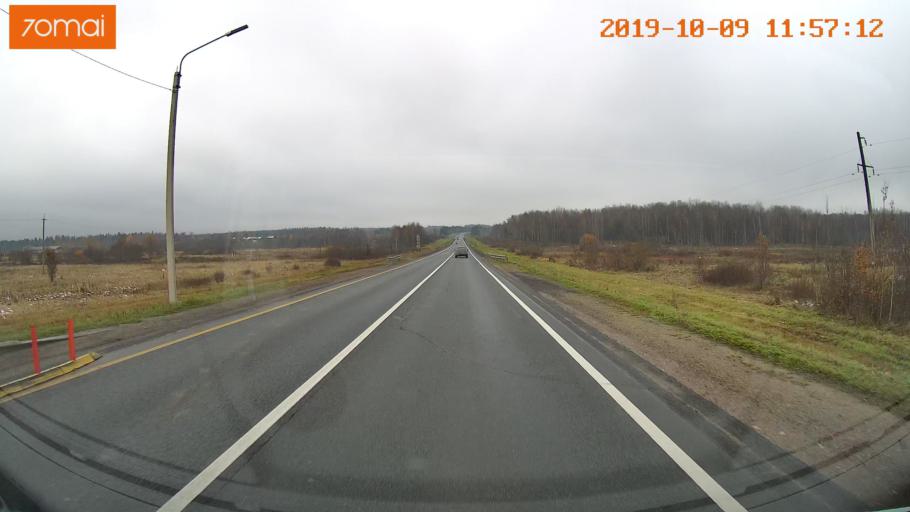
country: RU
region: Vologda
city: Gryazovets
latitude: 58.7353
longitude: 40.2913
